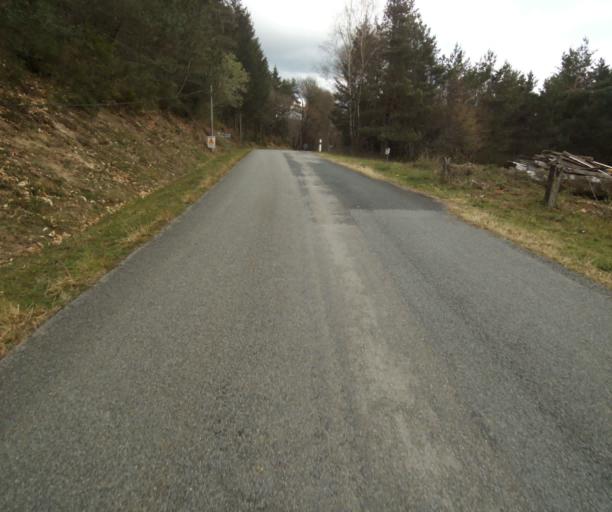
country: FR
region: Limousin
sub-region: Departement de la Correze
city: Correze
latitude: 45.3179
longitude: 1.9539
